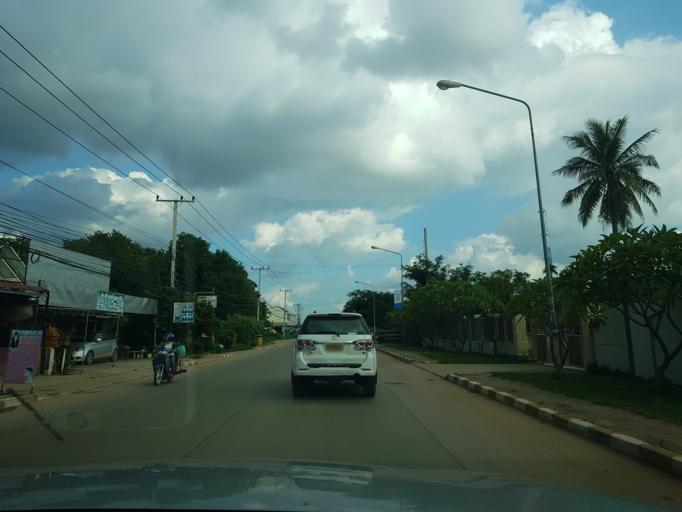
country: TH
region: Nong Khai
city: Si Chiang Mai
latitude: 17.9764
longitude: 102.5424
